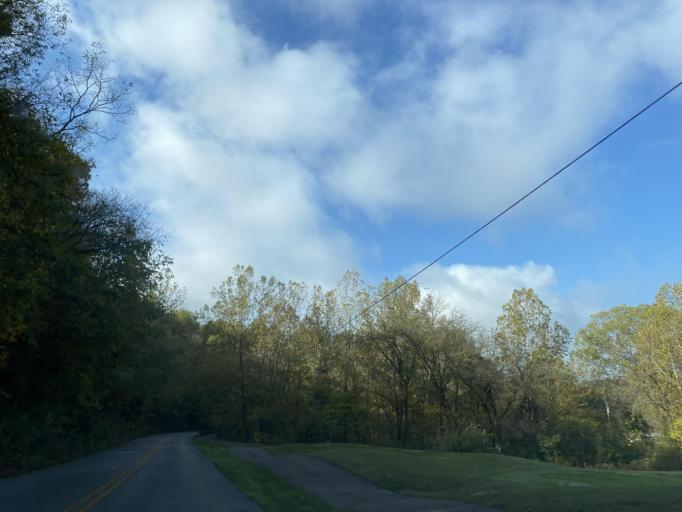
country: US
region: Kentucky
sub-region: Pendleton County
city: Falmouth
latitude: 38.7195
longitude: -84.2953
